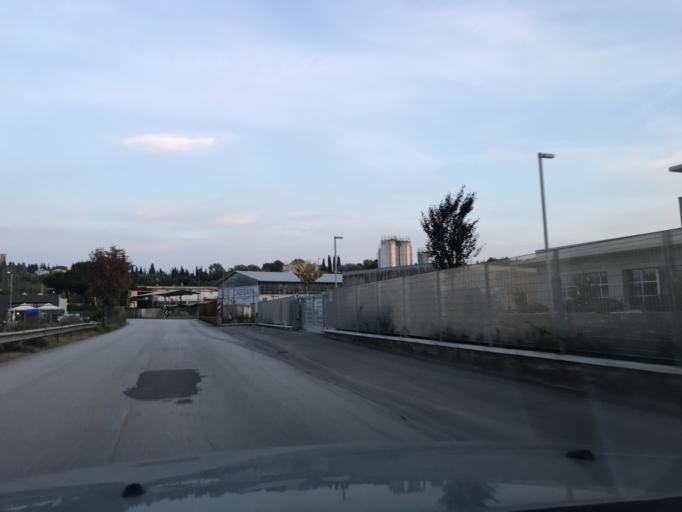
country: IT
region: Umbria
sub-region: Provincia di Perugia
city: Via Lippia
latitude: 43.0879
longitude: 12.4628
